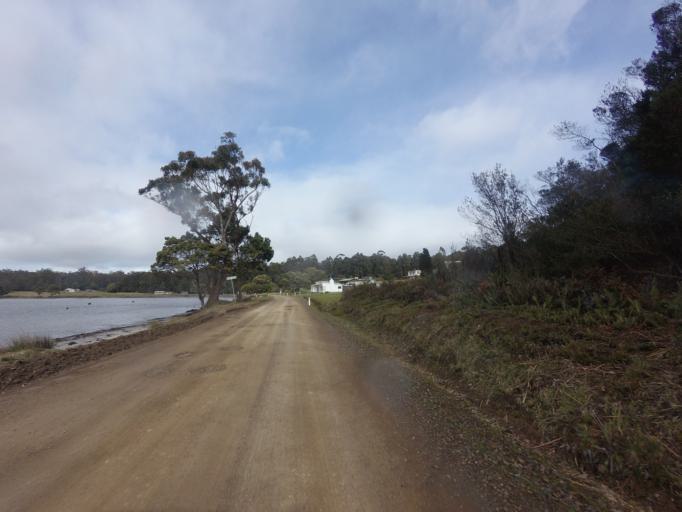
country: AU
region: Tasmania
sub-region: Huon Valley
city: Geeveston
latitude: -43.5330
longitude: 146.8923
